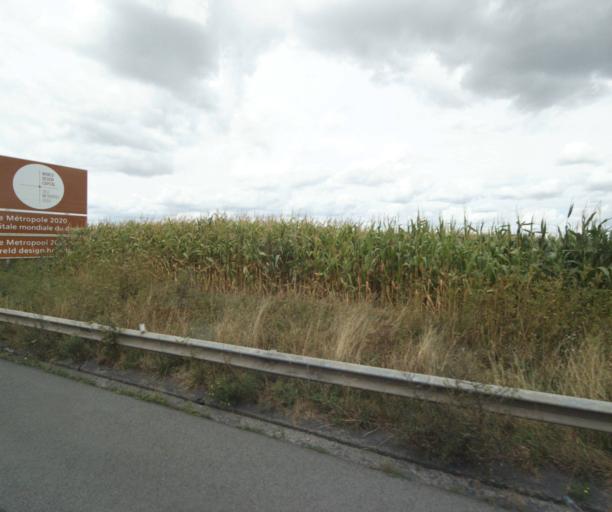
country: FR
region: Nord-Pas-de-Calais
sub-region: Departement du Nord
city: Camphin-en-Pevele
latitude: 50.6016
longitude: 3.2600
